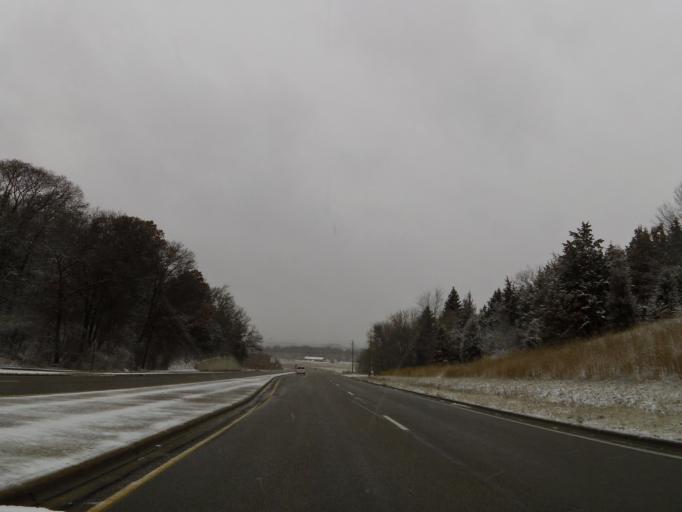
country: US
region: Minnesota
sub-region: Scott County
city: Prior Lake
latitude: 44.7632
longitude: -93.4034
